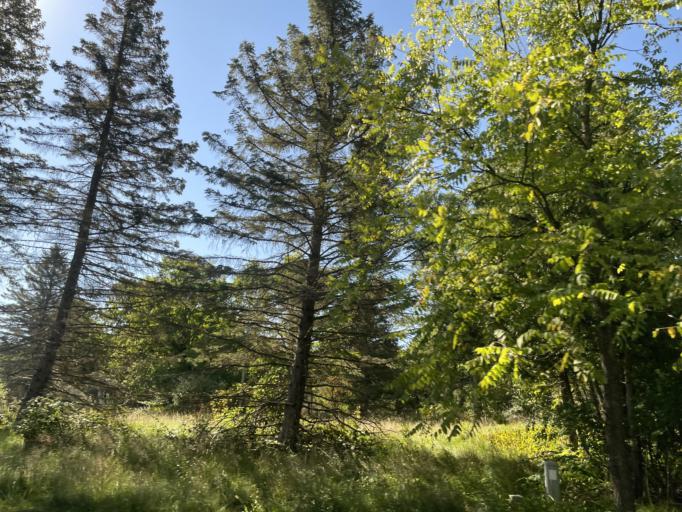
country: US
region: Michigan
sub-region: Benzie County
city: Beulah
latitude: 44.6175
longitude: -86.0861
